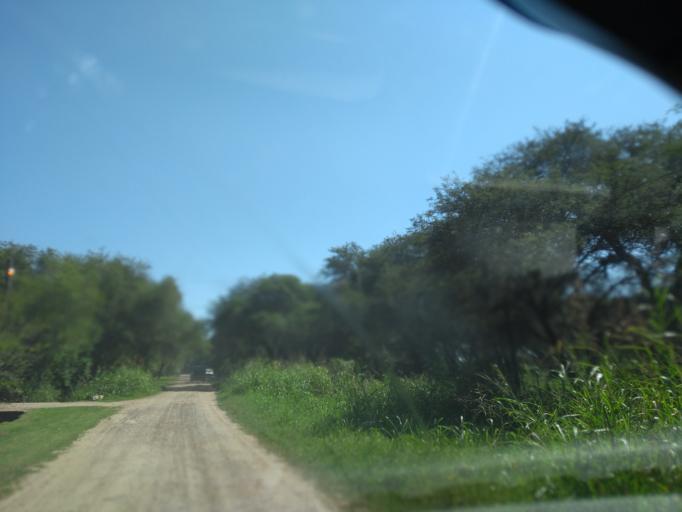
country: AR
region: Chaco
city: Resistencia
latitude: -27.4292
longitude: -58.9435
